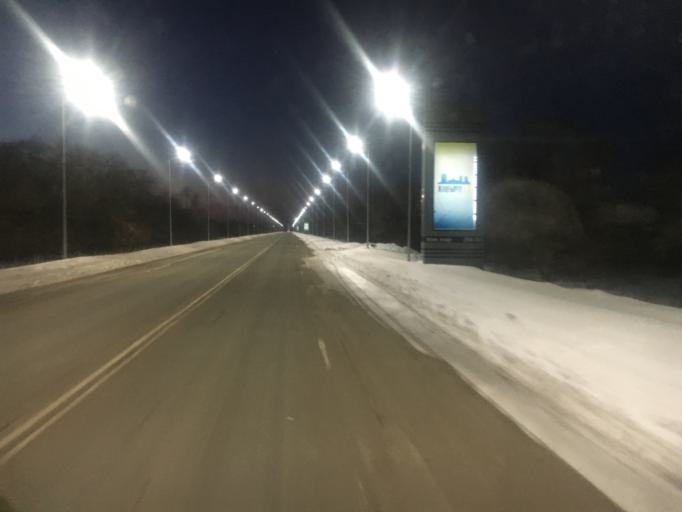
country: KZ
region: Batys Qazaqstan
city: Oral
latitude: 51.1574
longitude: 51.5339
